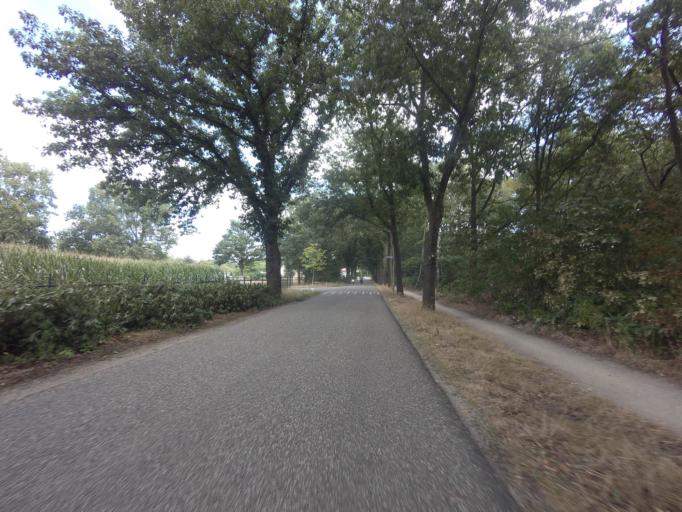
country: NL
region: North Brabant
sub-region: Gemeente Landerd
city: Schaijk
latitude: 51.7349
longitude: 5.6329
